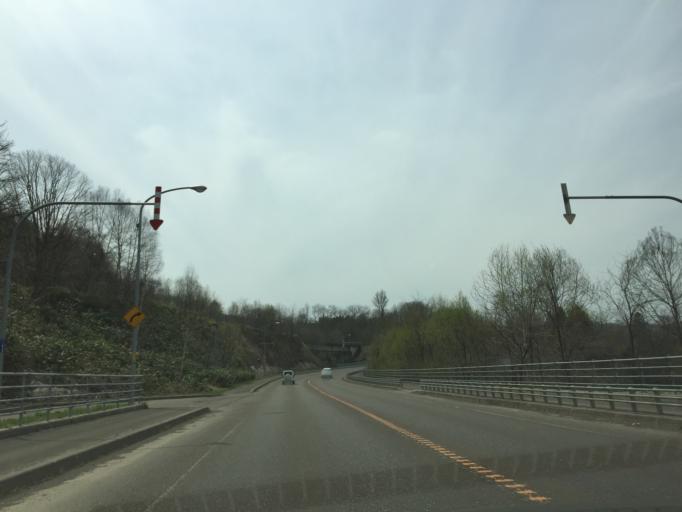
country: JP
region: Hokkaido
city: Akabira
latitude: 43.5366
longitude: 142.1002
